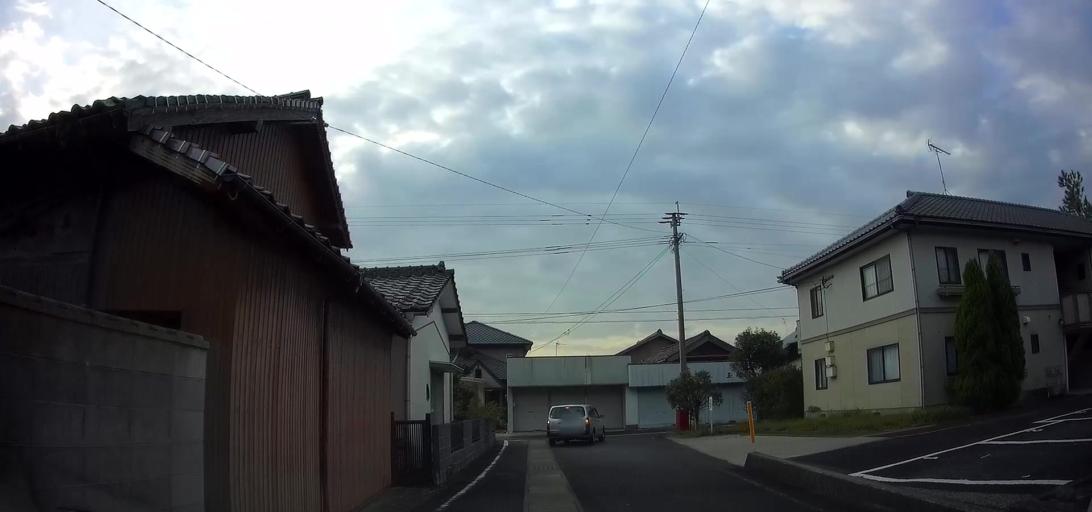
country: JP
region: Nagasaki
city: Shimabara
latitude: 32.6567
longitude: 130.2506
